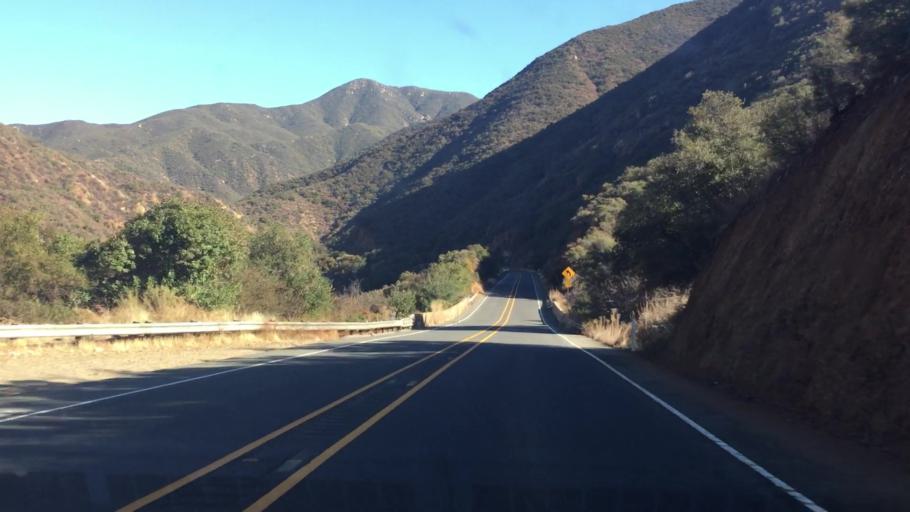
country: US
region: California
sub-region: Orange County
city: Coto De Caza
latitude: 33.5927
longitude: -117.4773
